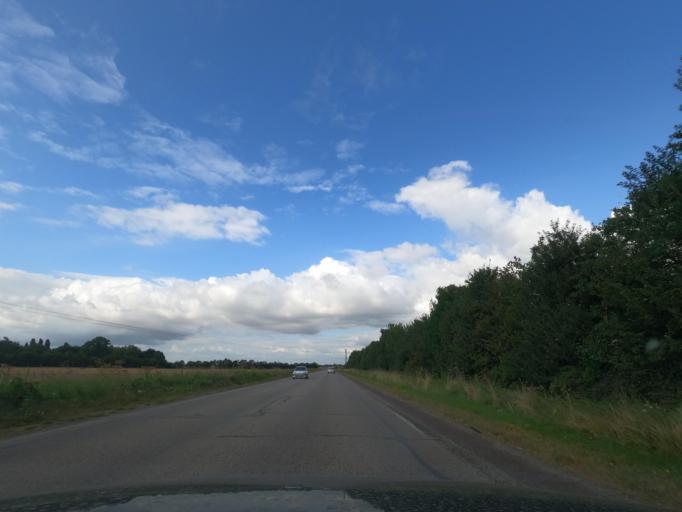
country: FR
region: Haute-Normandie
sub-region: Departement de l'Eure
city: Broglie
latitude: 49.0010
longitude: 0.5113
